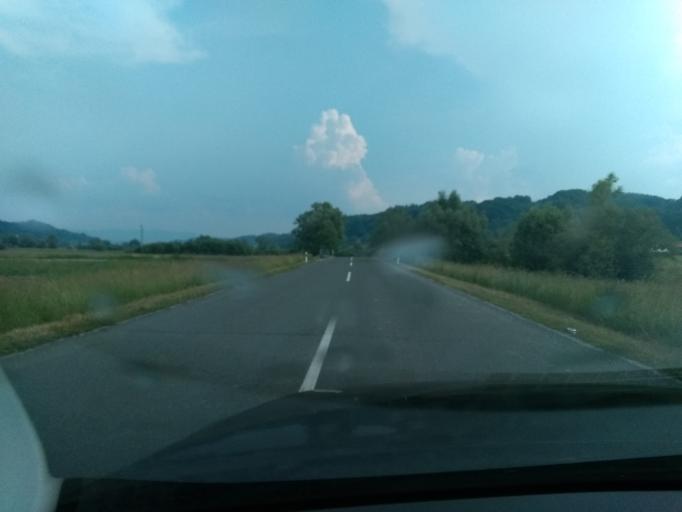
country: HR
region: Krapinsko-Zagorska
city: Pregrada
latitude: 46.0665
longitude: 15.7938
